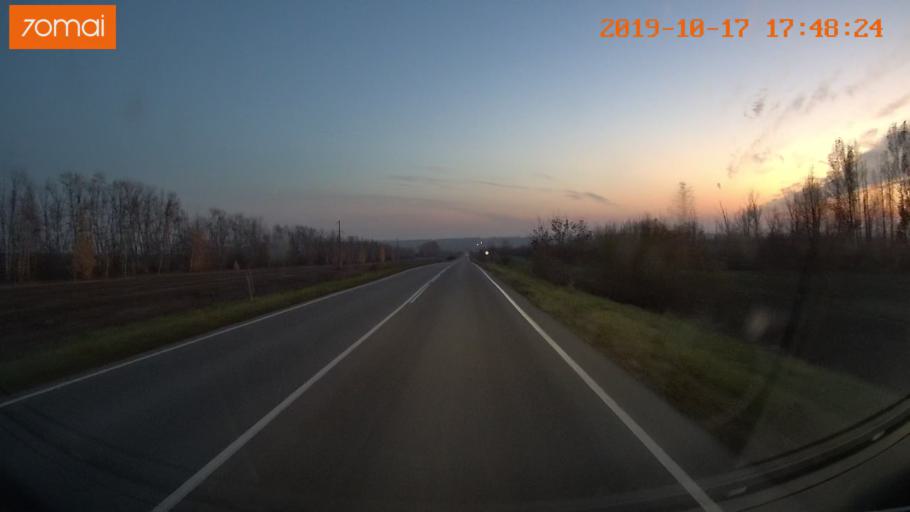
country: RU
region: Tula
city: Yepifan'
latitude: 53.6930
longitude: 38.6952
